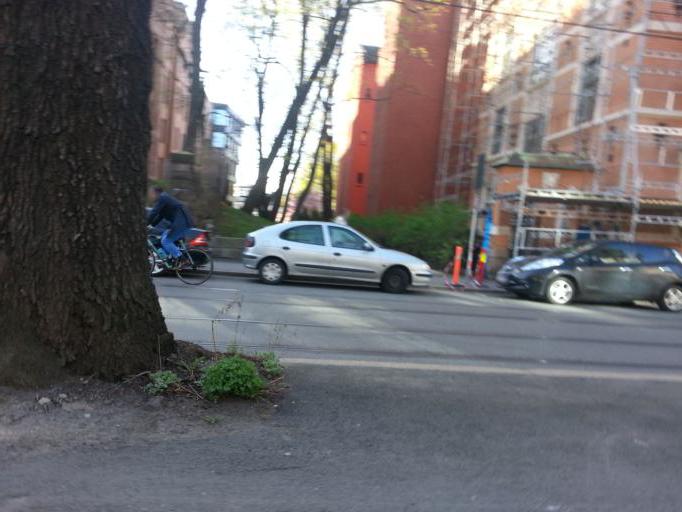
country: NO
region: Oslo
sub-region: Oslo
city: Oslo
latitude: 59.9144
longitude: 10.7166
